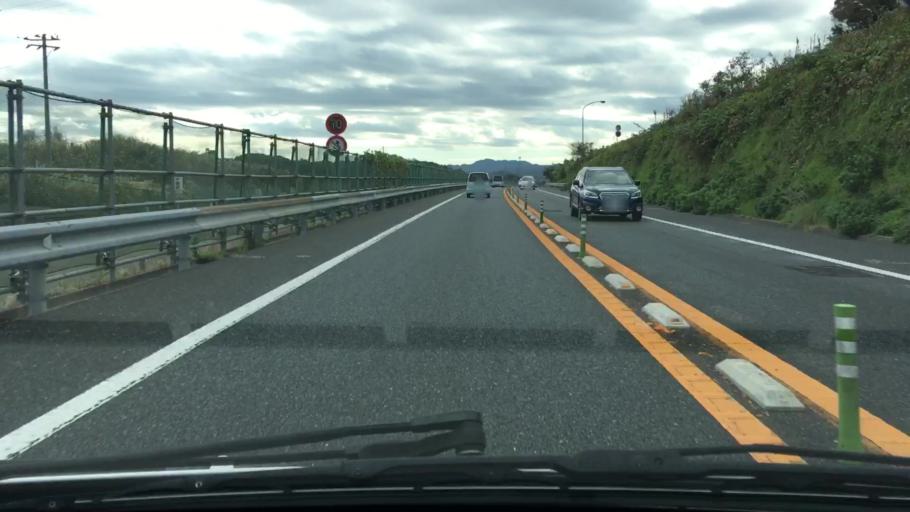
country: JP
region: Chiba
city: Kimitsu
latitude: 35.2394
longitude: 139.8884
